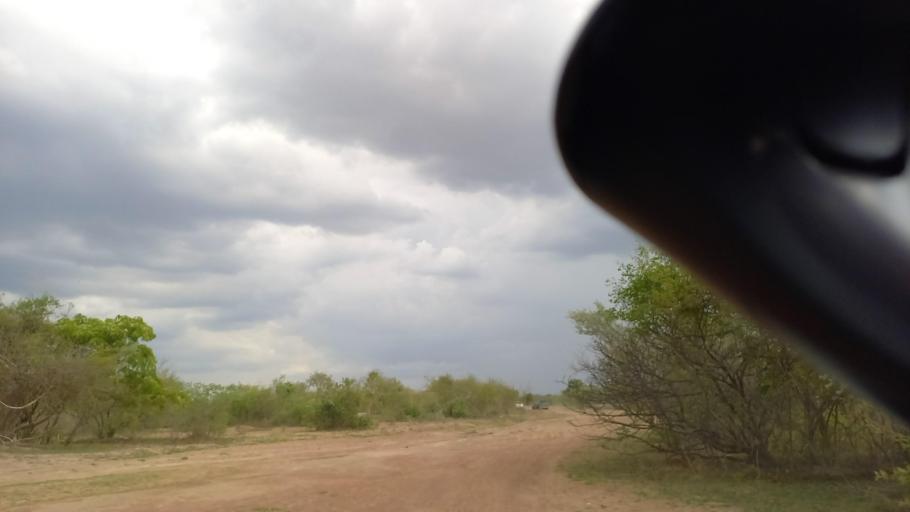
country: ZM
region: Lusaka
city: Kafue
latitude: -15.8517
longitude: 28.1117
